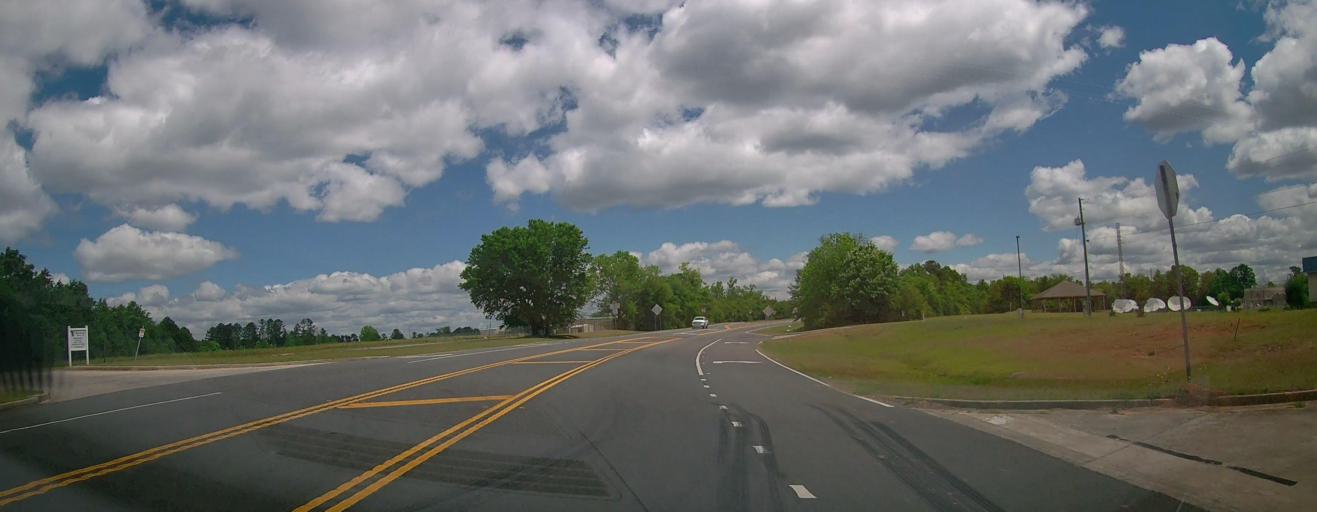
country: US
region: Georgia
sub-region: Houston County
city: Centerville
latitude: 32.7276
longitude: -83.6590
